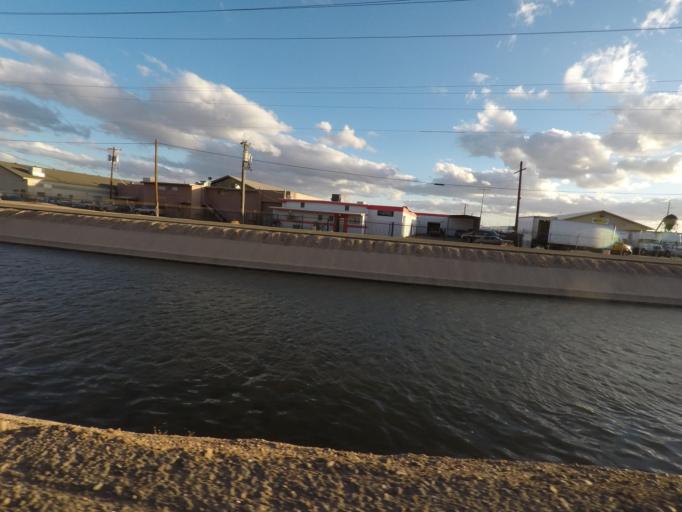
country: US
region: Arizona
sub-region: Maricopa County
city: Phoenix
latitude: 33.4901
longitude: -112.1242
